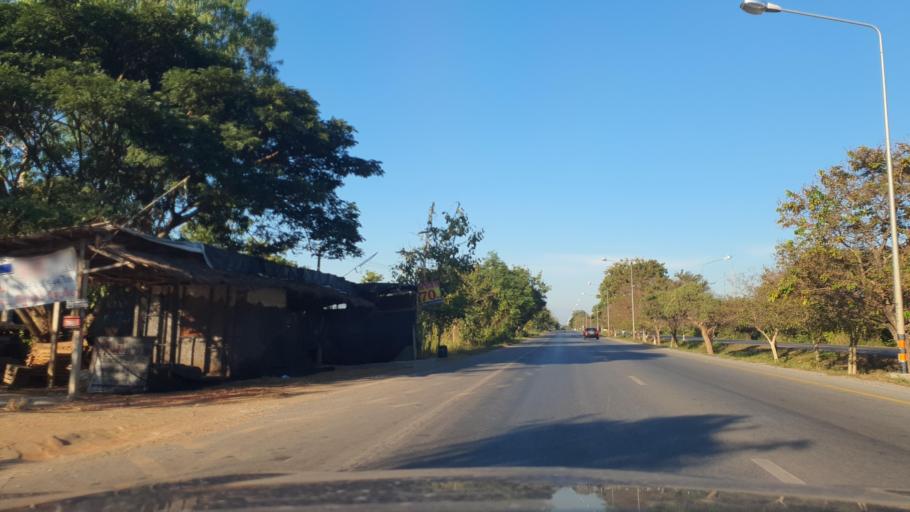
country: TH
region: Phitsanulok
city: Phitsanulok
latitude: 16.8650
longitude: 100.2322
